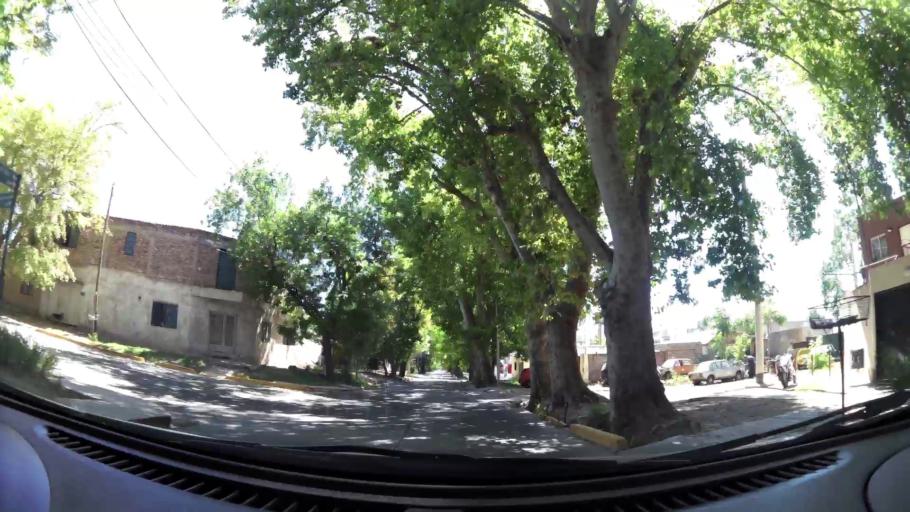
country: AR
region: Mendoza
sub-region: Departamento de Godoy Cruz
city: Godoy Cruz
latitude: -32.9525
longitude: -68.8421
